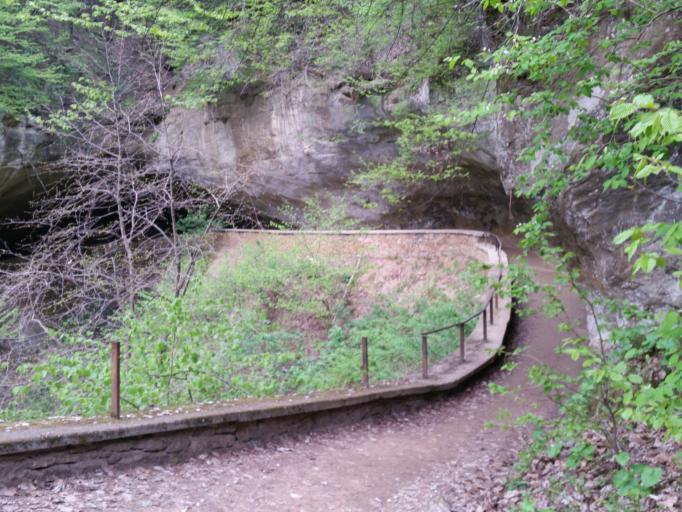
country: RU
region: Stavropol'skiy
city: Kislovodsk
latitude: 43.8944
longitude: 42.7571
